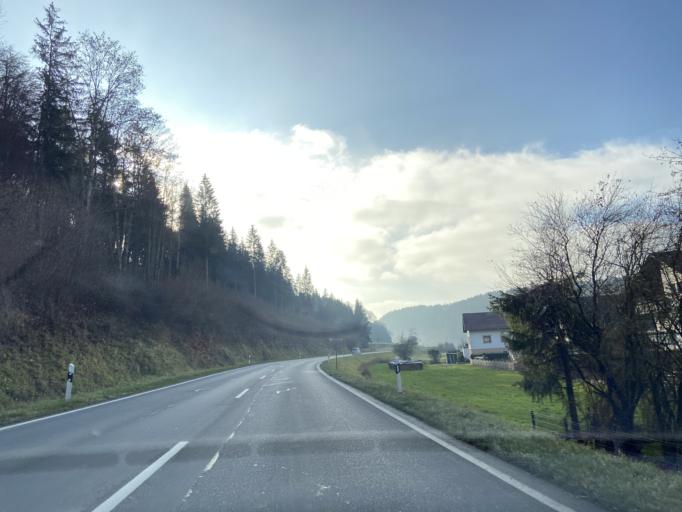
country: DE
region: Baden-Wuerttemberg
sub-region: Tuebingen Region
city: Hettingen
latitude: 48.2102
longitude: 9.2303
